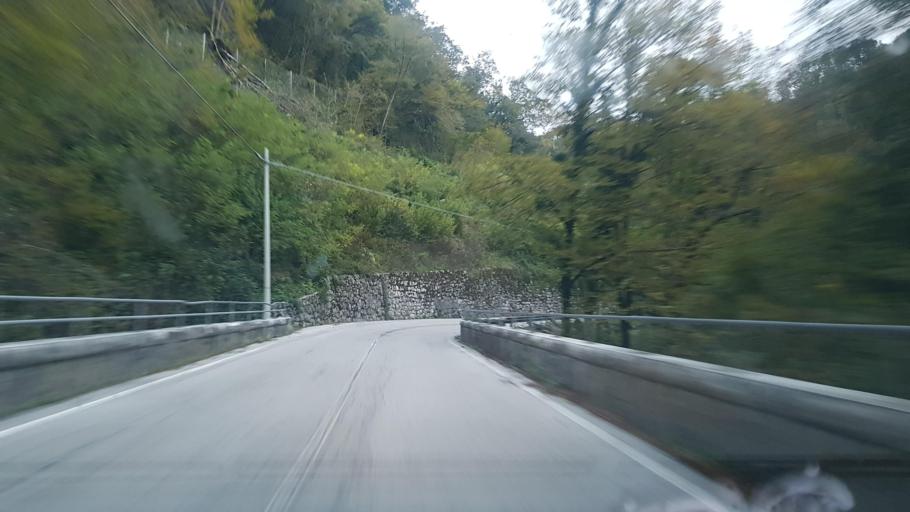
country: IT
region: Friuli Venezia Giulia
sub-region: Provincia di Pordenone
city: Anduins
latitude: 46.2710
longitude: 12.9474
